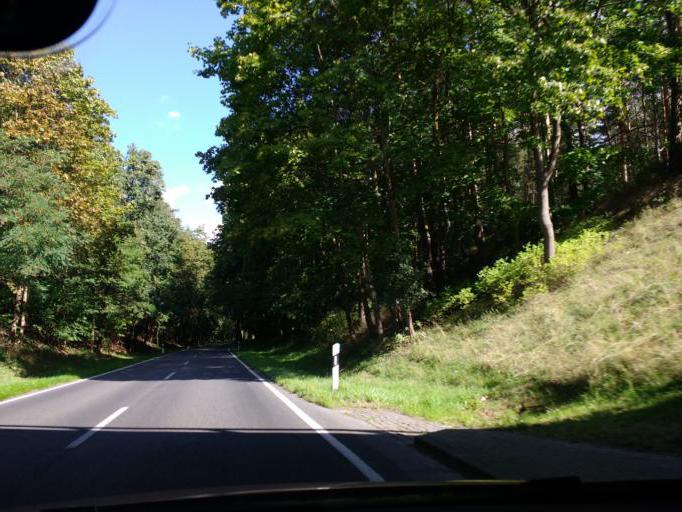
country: DE
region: Brandenburg
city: Bestensee
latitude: 52.2169
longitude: 13.6006
